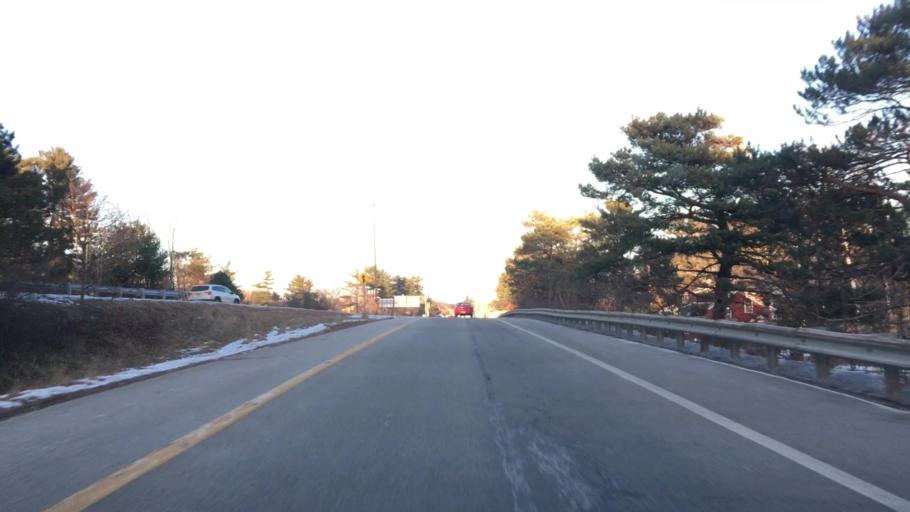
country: US
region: Maine
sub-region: York County
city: Kittery
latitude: 43.1068
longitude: -70.7410
